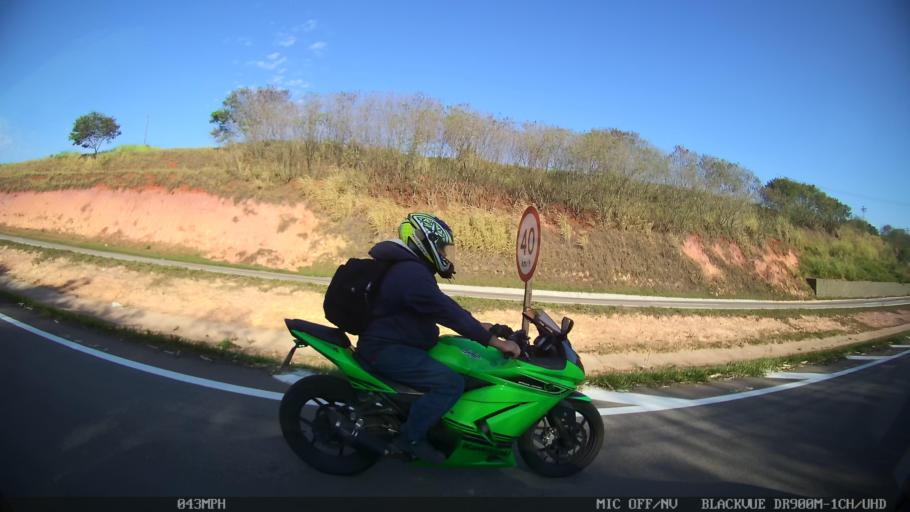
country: BR
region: Sao Paulo
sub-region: Piracicaba
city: Piracicaba
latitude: -22.6634
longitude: -47.6155
